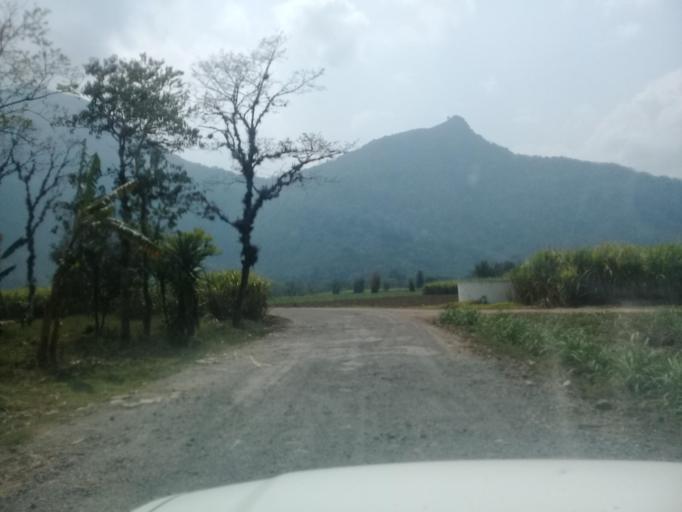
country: MX
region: Veracruz
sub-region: Ixtaczoquitlan
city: Capoluca
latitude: 18.8127
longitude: -96.9919
